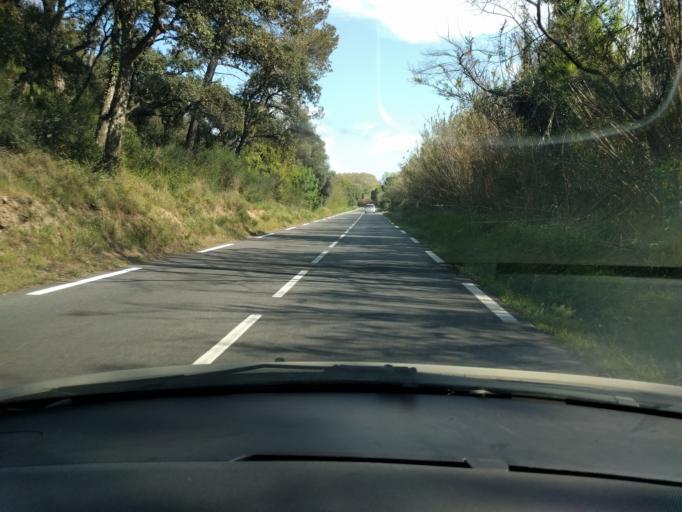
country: FR
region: Provence-Alpes-Cote d'Azur
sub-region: Departement du Var
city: Hyeres
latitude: 43.1638
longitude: 6.1212
